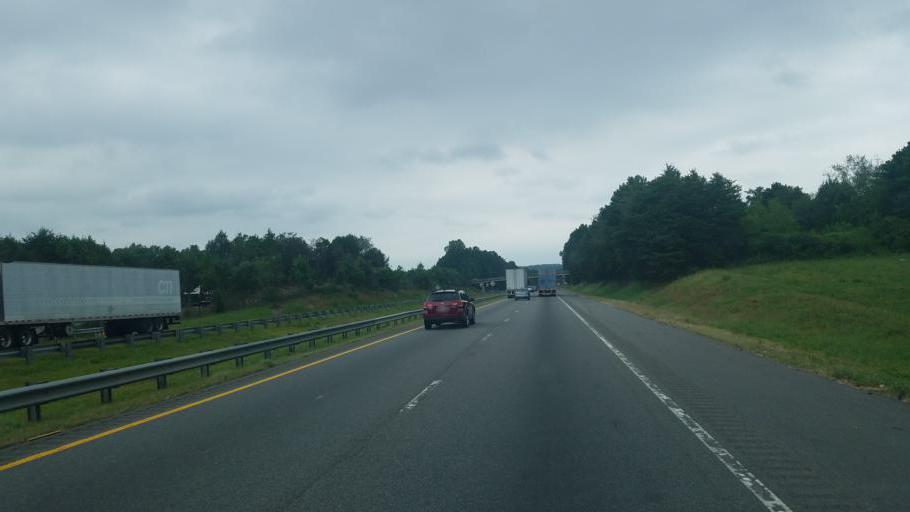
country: US
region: North Carolina
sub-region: Iredell County
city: Mooresville
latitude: 35.6211
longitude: -80.8587
